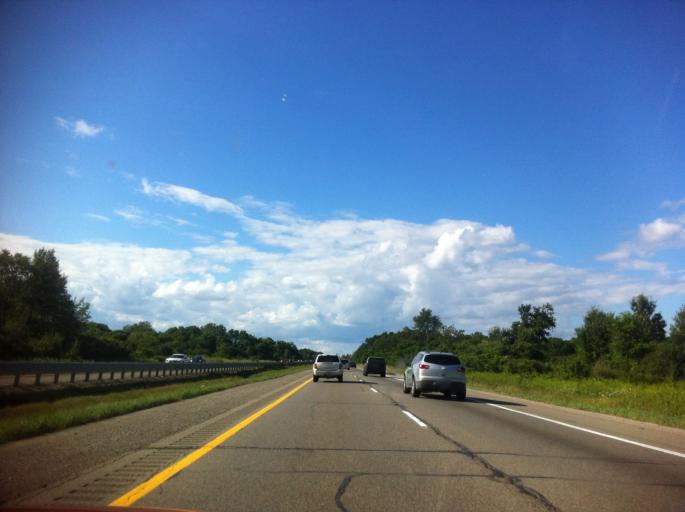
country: US
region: Michigan
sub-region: Washtenaw County
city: Ann Arbor
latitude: 42.3325
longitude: -83.7433
